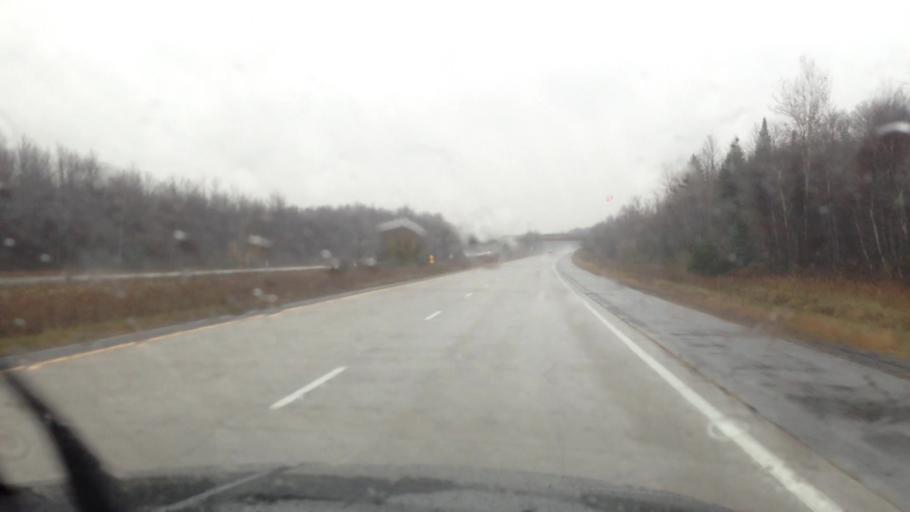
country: CA
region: Ontario
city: Hawkesbury
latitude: 45.4931
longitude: -74.6171
